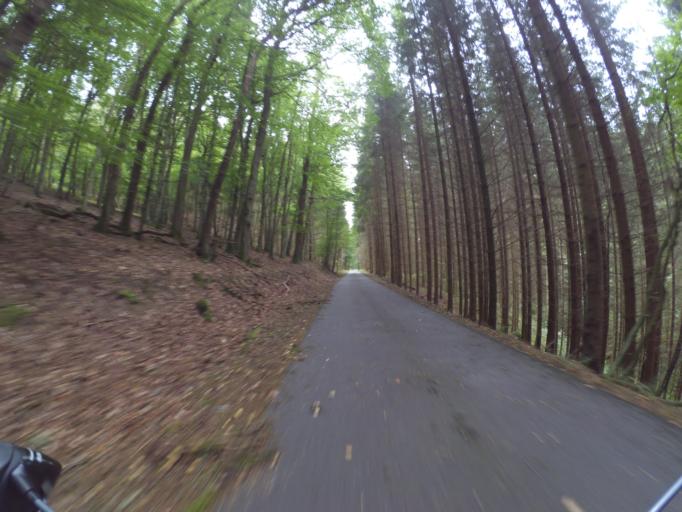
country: DE
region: Rheinland-Pfalz
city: Beilingen
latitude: 49.9577
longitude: 6.6721
